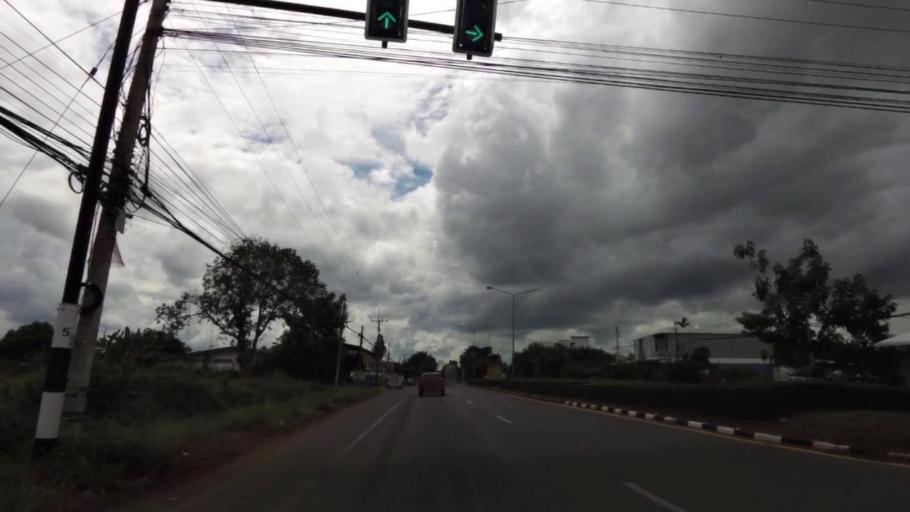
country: TH
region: Nakhon Sawan
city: Phai Sali
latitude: 15.5925
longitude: 100.6568
